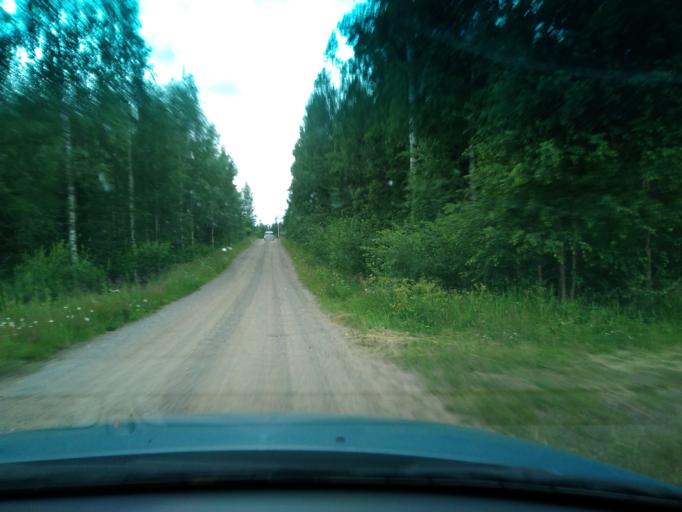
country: FI
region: Central Finland
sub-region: Saarijaervi-Viitasaari
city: Karstula
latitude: 62.7878
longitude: 24.9486
